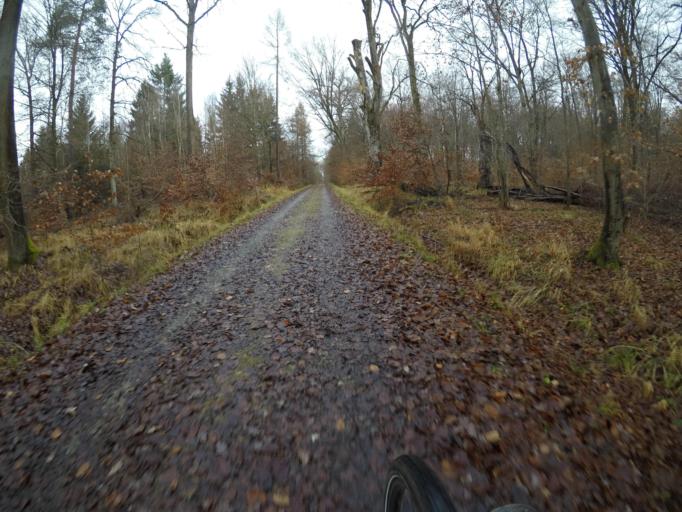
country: DE
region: Baden-Wuerttemberg
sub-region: Regierungsbezirk Stuttgart
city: Gerlingen
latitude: 48.7586
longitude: 9.0819
